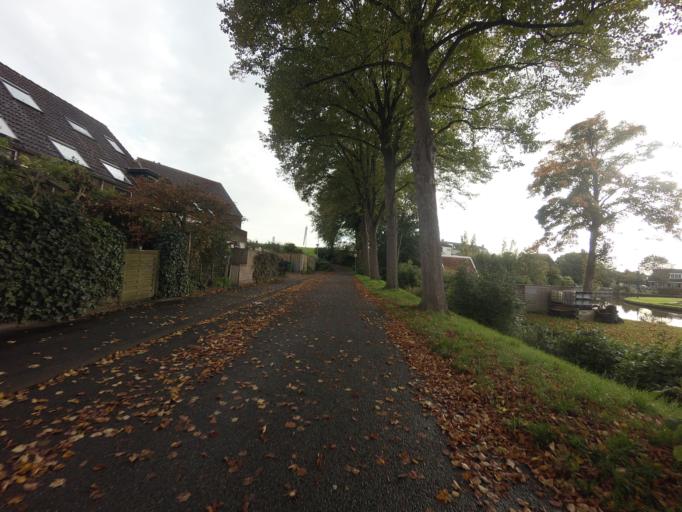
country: NL
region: South Holland
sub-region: Gemeente Schoonhoven
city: Schoonhoven
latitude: 51.9434
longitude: 4.8469
